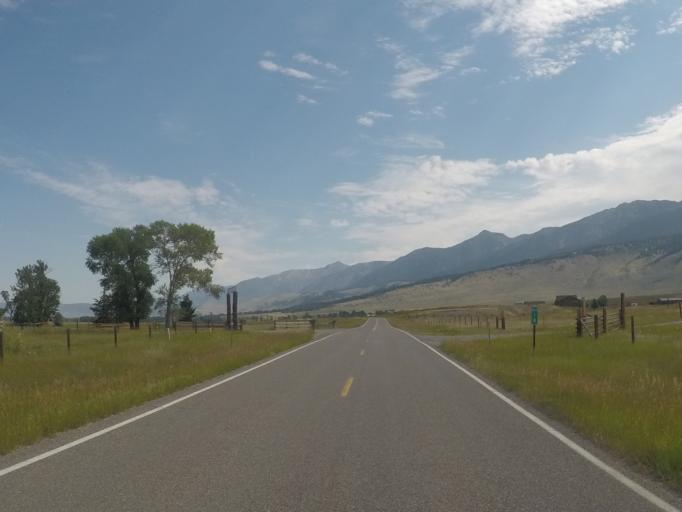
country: US
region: Montana
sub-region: Park County
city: Livingston
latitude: 45.4234
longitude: -110.6258
